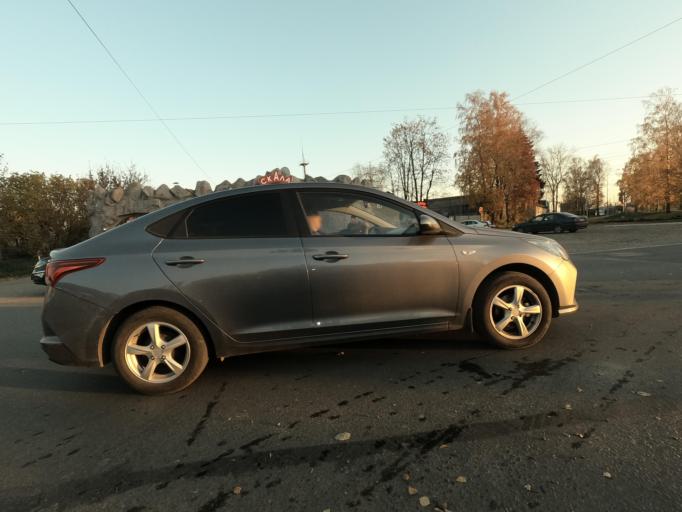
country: RU
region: Leningrad
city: Kirovsk
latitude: 59.8716
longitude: 30.9873
